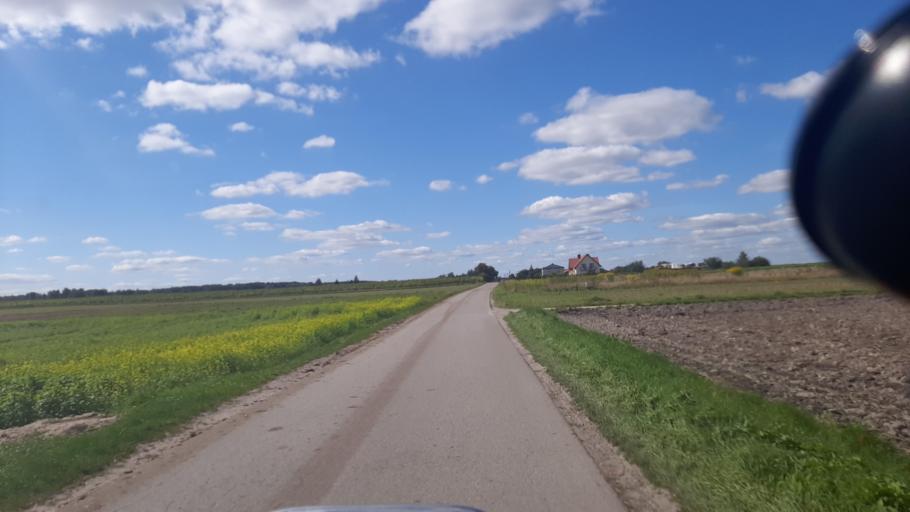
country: PL
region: Lublin Voivodeship
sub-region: Powiat lubartowski
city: Kamionka
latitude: 51.4050
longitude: 22.4074
